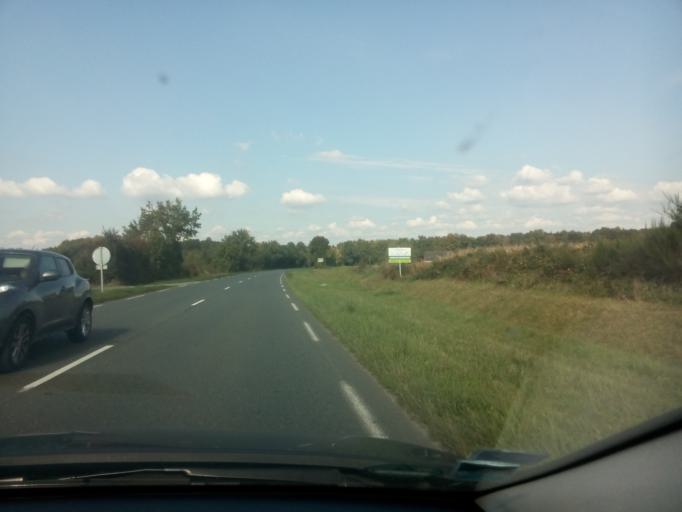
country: FR
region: Pays de la Loire
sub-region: Departement de Maine-et-Loire
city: Ecouflant
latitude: 47.5170
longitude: -0.5043
